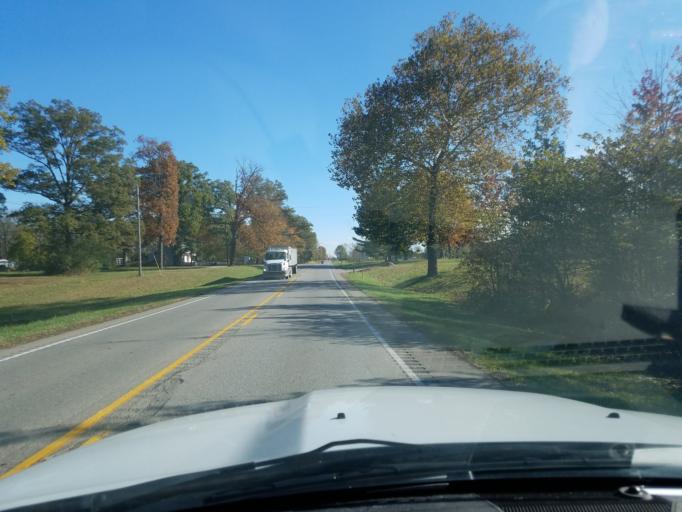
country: US
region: Indiana
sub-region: Jennings County
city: Country Squire Lakes
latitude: 38.9741
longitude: -85.7538
